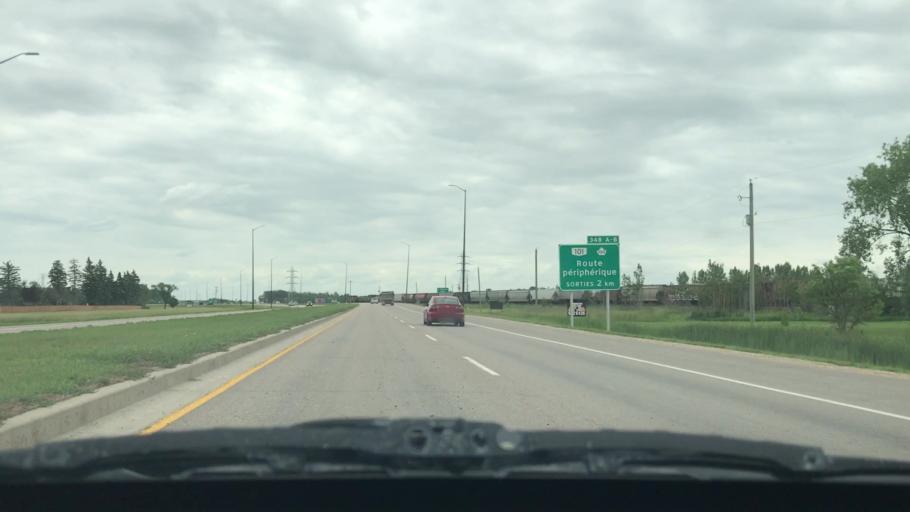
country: CA
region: Manitoba
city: Winnipeg
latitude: 49.8445
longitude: -96.9928
